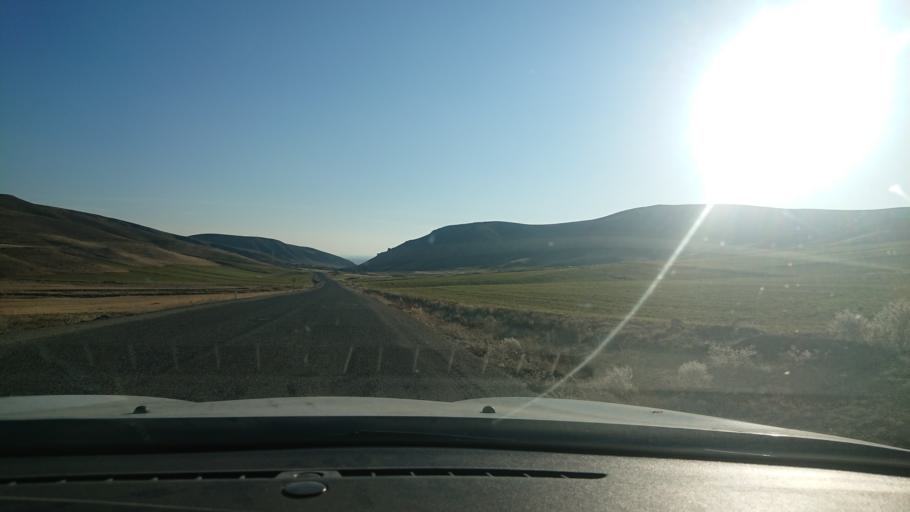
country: TR
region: Aksaray
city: Acipinar
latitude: 38.7005
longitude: 33.7526
